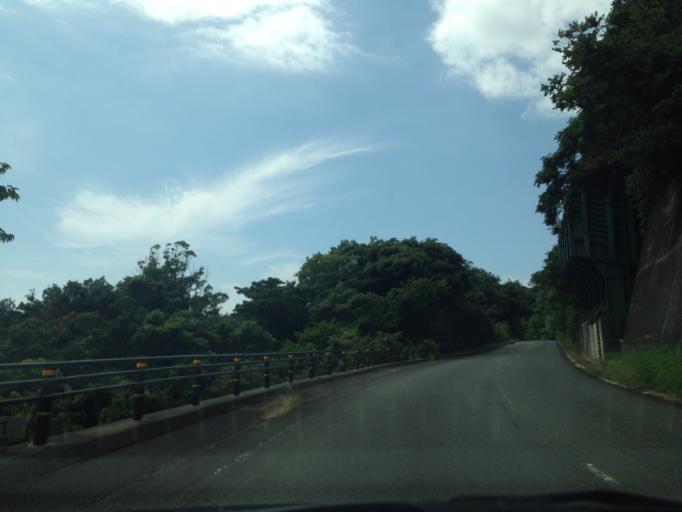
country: JP
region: Shizuoka
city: Shimoda
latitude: 34.6724
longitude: 138.7873
